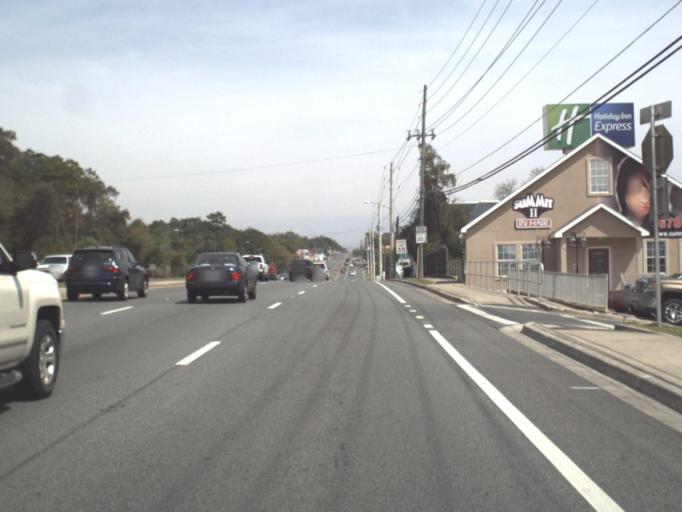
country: US
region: Florida
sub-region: Okaloosa County
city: Niceville
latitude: 30.5217
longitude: -86.4917
